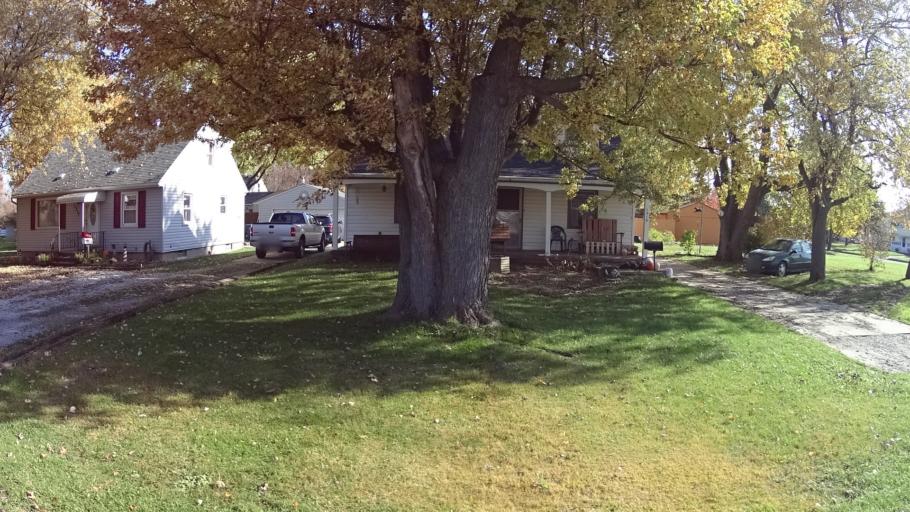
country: US
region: Ohio
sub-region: Lorain County
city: Lorain
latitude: 41.4696
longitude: -82.1556
